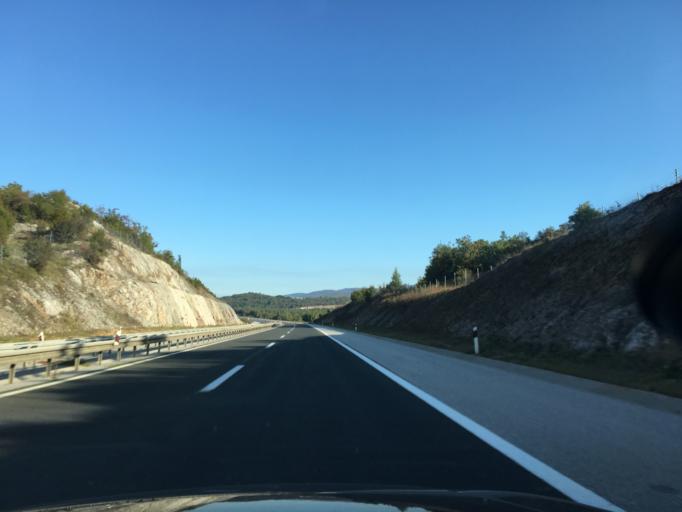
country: HR
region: Licko-Senjska
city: Gospic
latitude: 44.7202
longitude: 15.3864
